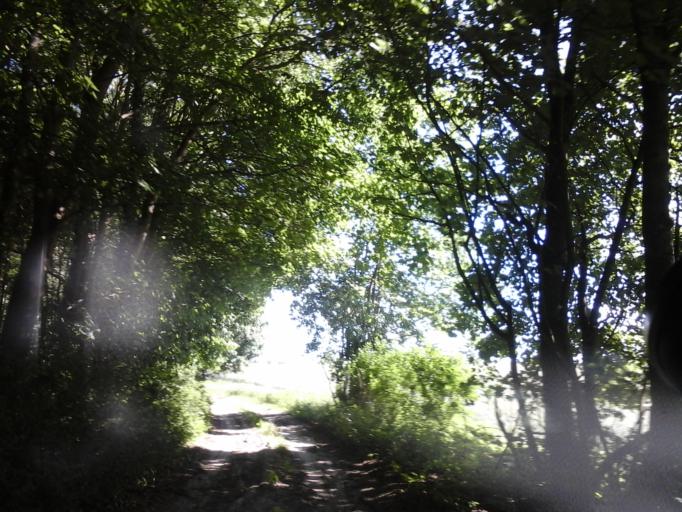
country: PL
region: West Pomeranian Voivodeship
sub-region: Powiat choszczenski
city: Recz
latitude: 53.1833
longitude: 15.5399
